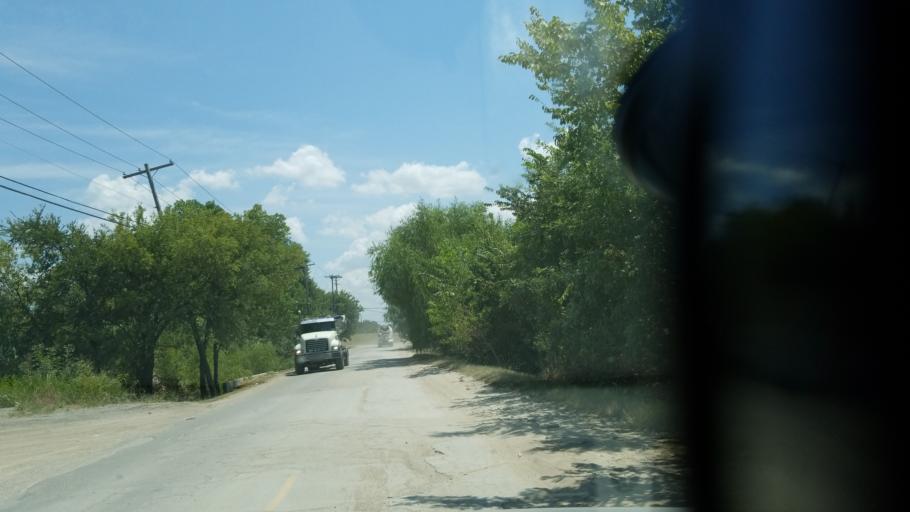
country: US
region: Texas
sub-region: Dallas County
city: Farmers Branch
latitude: 32.8726
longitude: -96.9198
